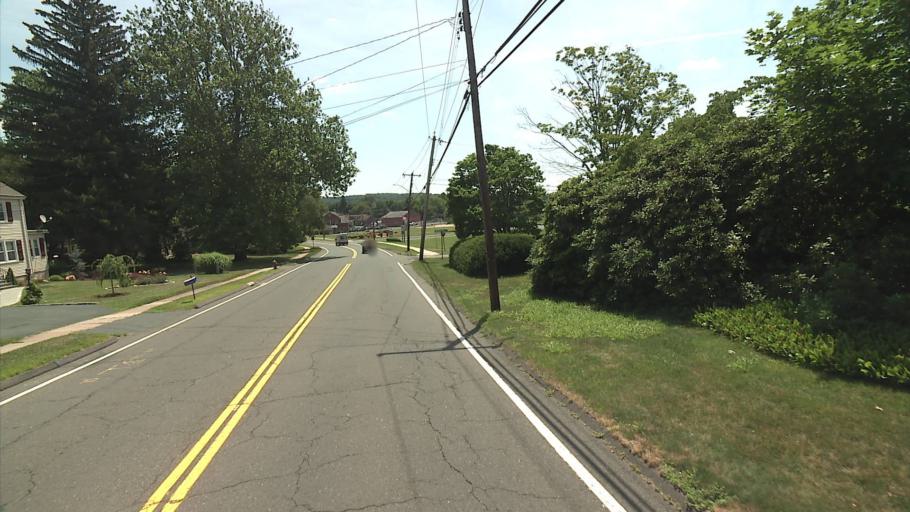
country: US
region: Connecticut
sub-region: Middlesex County
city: Cromwell
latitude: 41.5970
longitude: -72.6491
